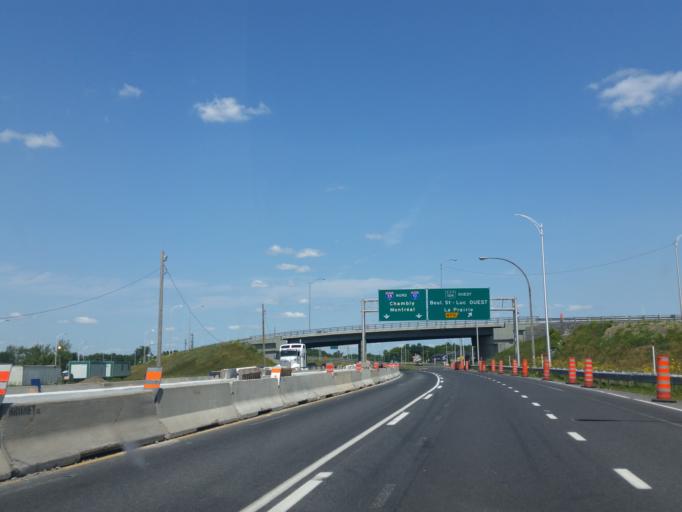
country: CA
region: Quebec
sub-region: Monteregie
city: Saint-Jean-sur-Richelieu
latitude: 45.3443
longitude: -73.2877
